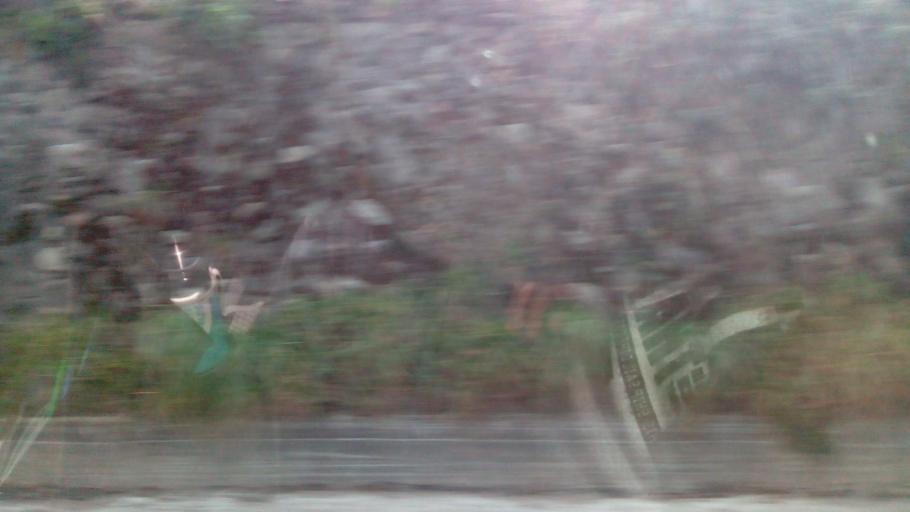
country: TW
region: Taiwan
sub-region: Hualien
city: Hualian
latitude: 24.3605
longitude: 121.3308
